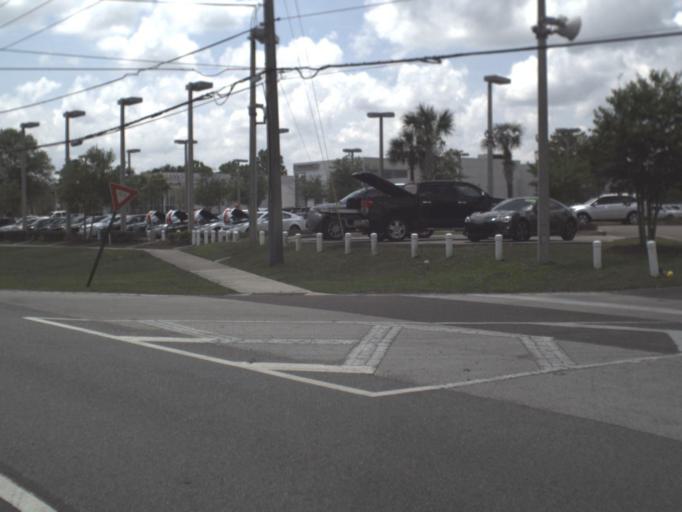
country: US
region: Florida
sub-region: Clay County
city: Bellair-Meadowbrook Terrace
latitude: 30.2166
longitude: -81.7371
